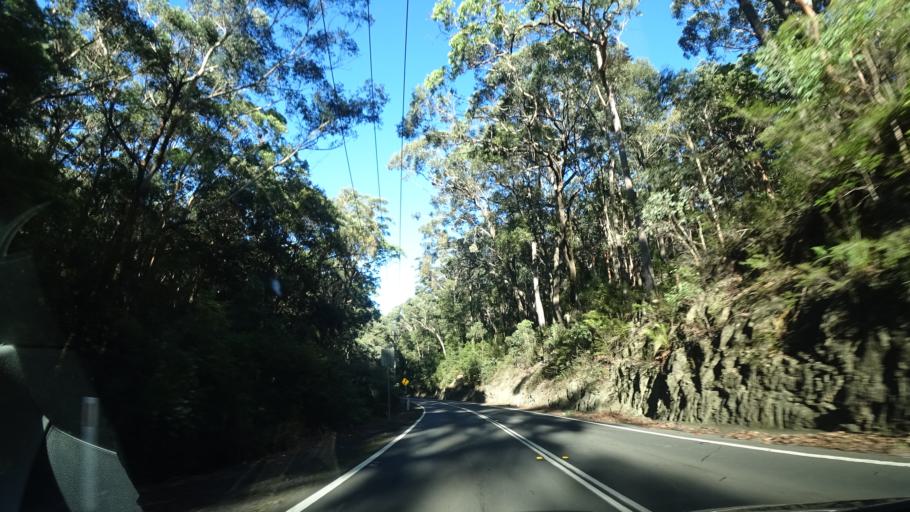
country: AU
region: New South Wales
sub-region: Hawkesbury
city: Richmond
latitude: -33.5178
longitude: 150.6243
